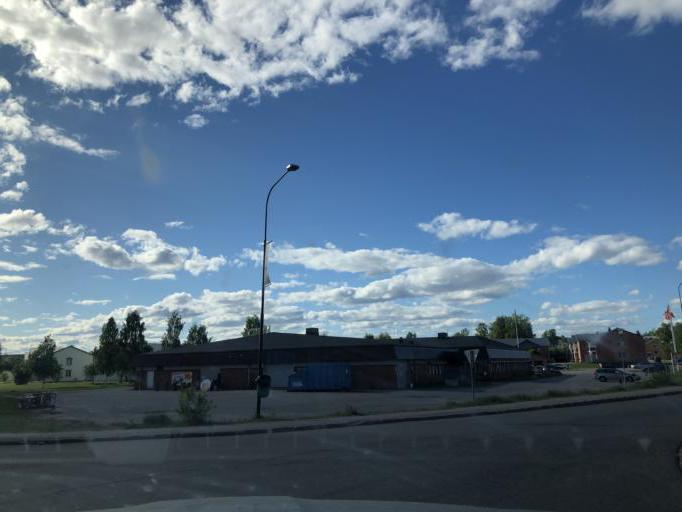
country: SE
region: Norrbotten
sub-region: Overkalix Kommun
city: OEverkalix
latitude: 66.3221
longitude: 22.8483
